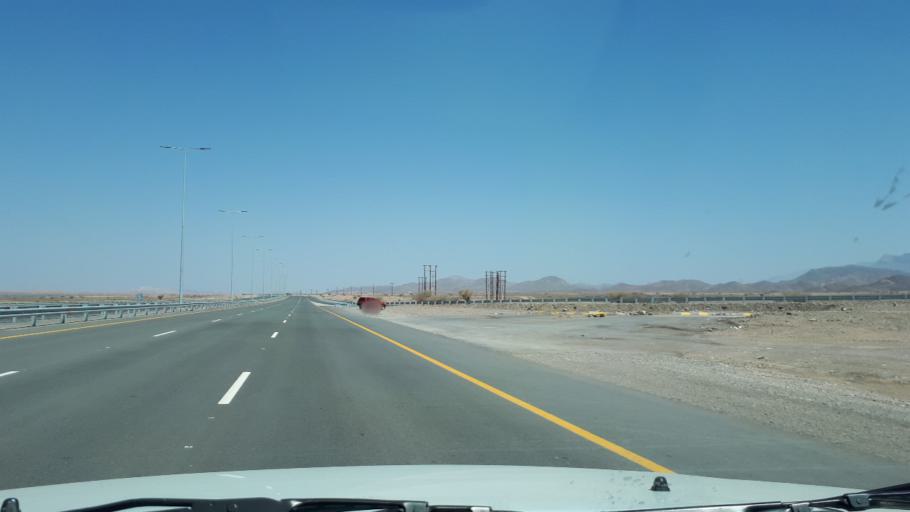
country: OM
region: Ash Sharqiyah
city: Badiyah
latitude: 22.4366
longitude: 59.0284
